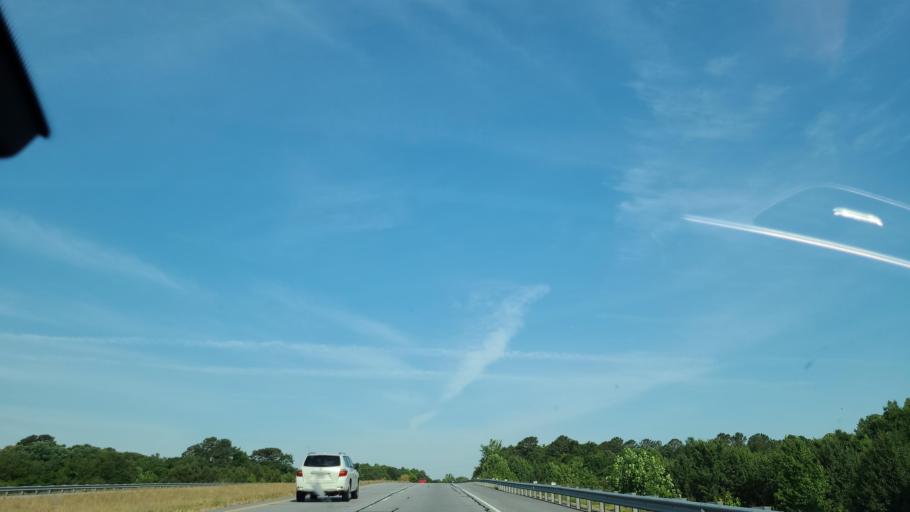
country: US
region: Georgia
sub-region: Jackson County
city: Nicholson
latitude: 34.0604
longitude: -83.4176
